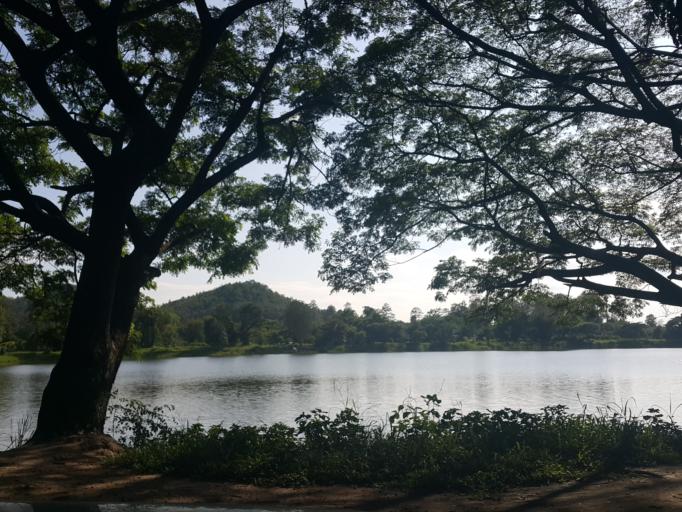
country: TH
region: Chiang Mai
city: San Kamphaeng
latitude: 18.7184
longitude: 99.1808
